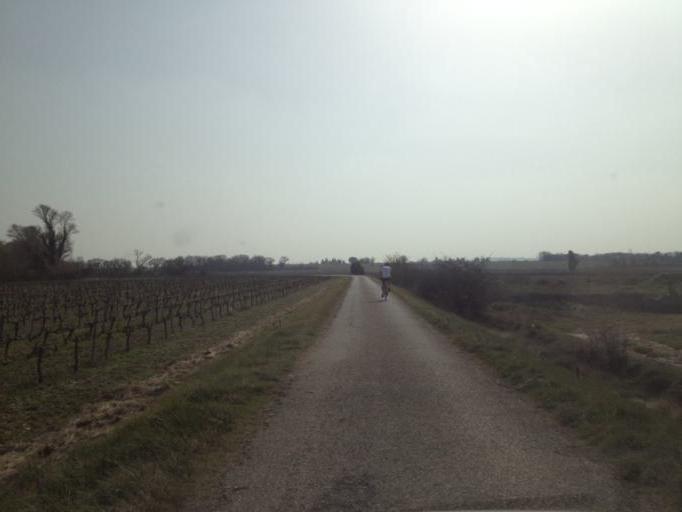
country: FR
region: Provence-Alpes-Cote d'Azur
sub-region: Departement du Vaucluse
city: Jonquieres
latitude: 44.0872
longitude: 4.9187
